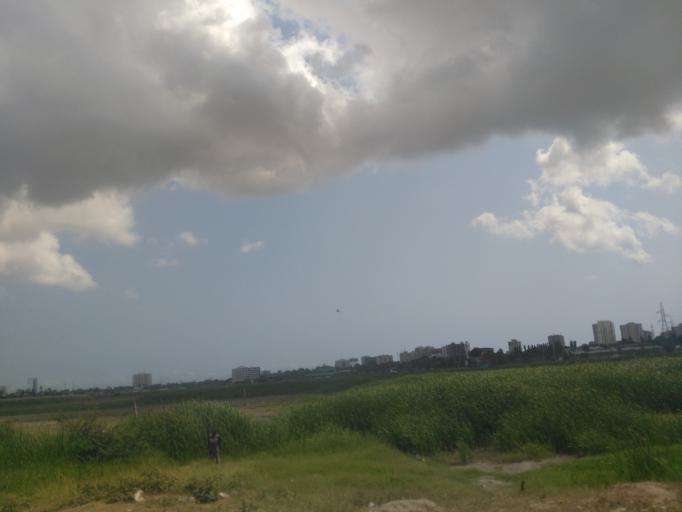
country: TZ
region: Dar es Salaam
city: Dar es Salaam
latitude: -6.8158
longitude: 39.2672
